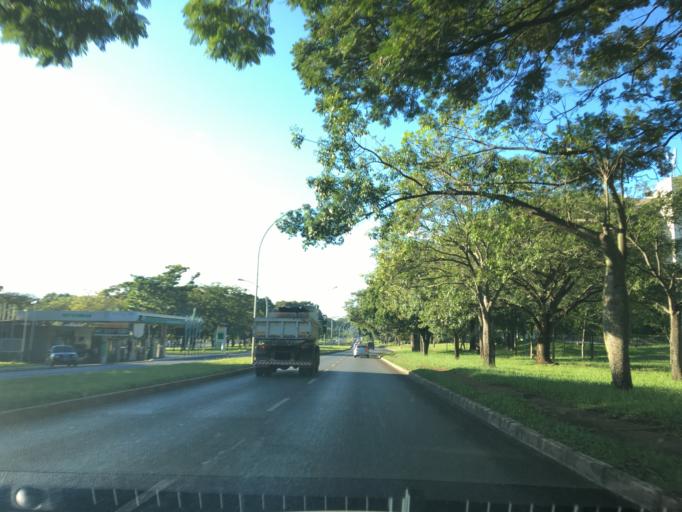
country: BR
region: Federal District
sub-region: Brasilia
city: Brasilia
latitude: -15.7476
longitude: -47.8895
